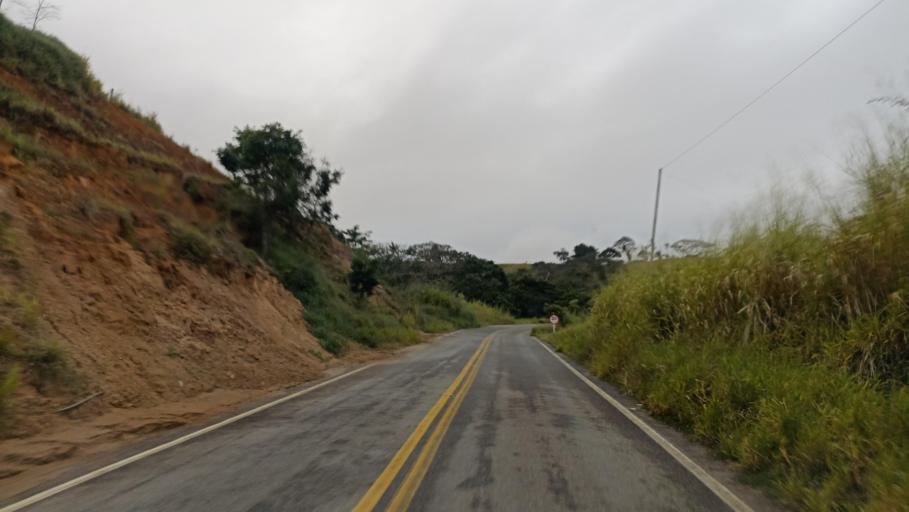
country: BR
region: Minas Gerais
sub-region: Joaima
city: Joaima
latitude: -16.6734
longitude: -40.5284
